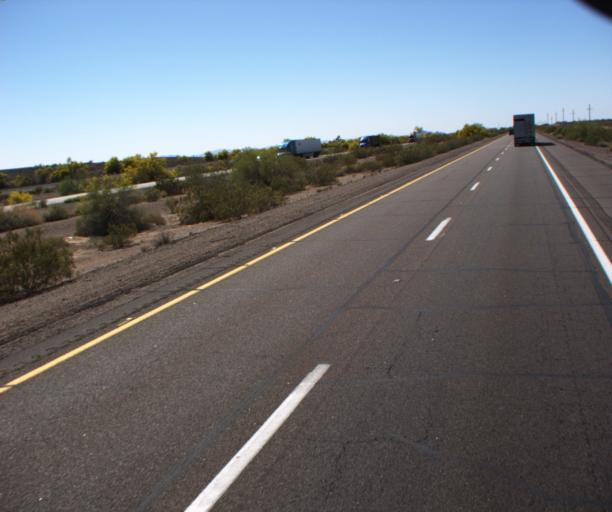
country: US
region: Arizona
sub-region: Maricopa County
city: Gila Bend
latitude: 32.8415
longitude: -113.3137
